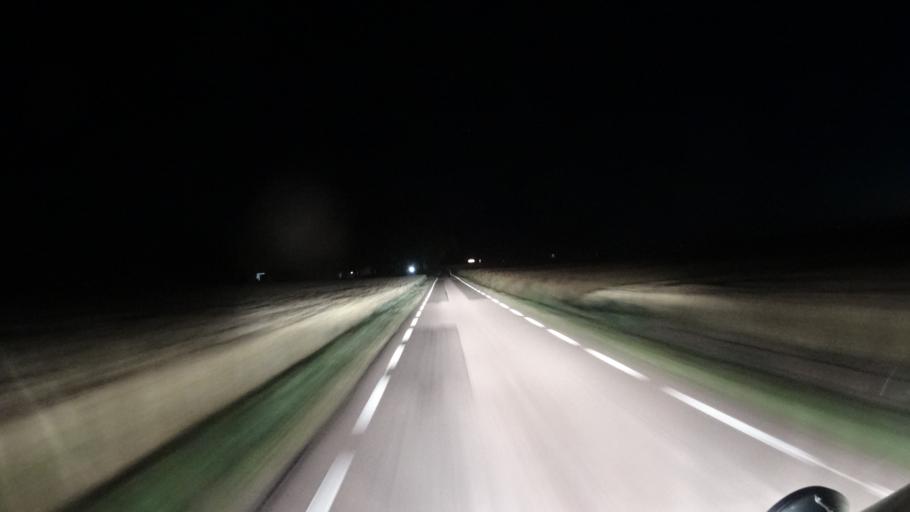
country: SE
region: OEstergoetland
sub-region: Vadstena Kommun
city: Herrestad
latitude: 58.3234
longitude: 14.8305
